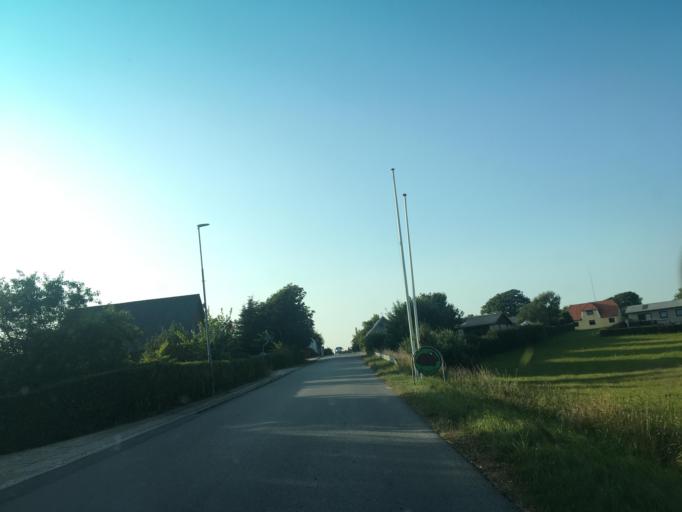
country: DK
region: North Denmark
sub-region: Thisted Kommune
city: Hurup
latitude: 56.8037
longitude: 8.4085
